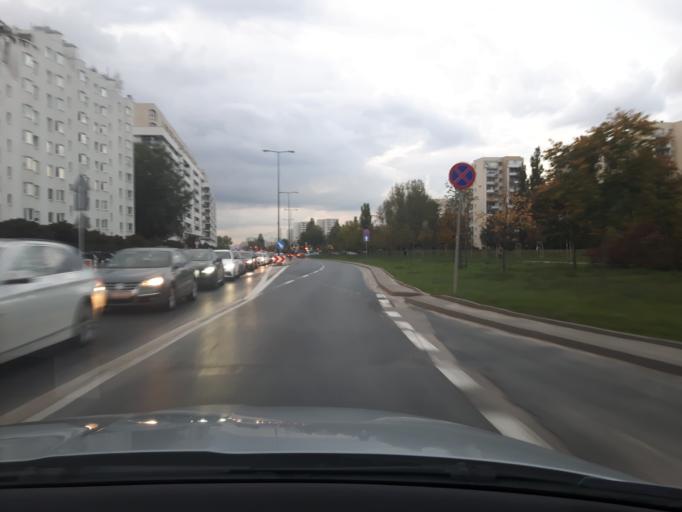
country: PL
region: Masovian Voivodeship
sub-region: Warszawa
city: Ursynow
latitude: 52.1460
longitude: 21.0513
